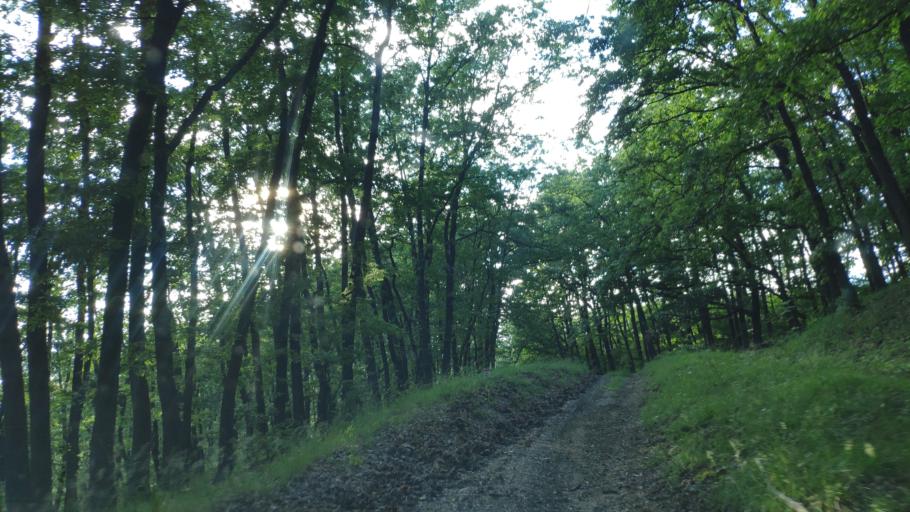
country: HU
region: Borsod-Abauj-Zemplen
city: Arlo
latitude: 48.2443
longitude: 20.1381
